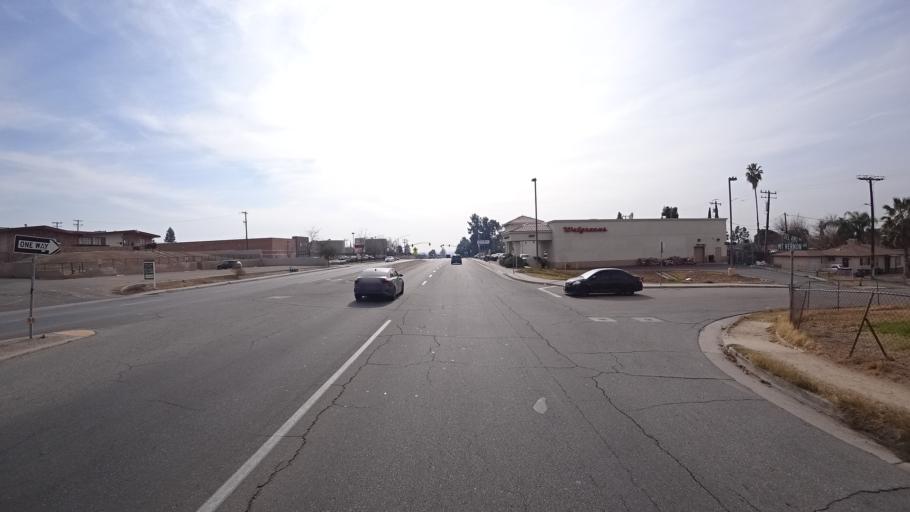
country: US
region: California
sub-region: Kern County
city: Bakersfield
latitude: 35.3919
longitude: -118.9675
